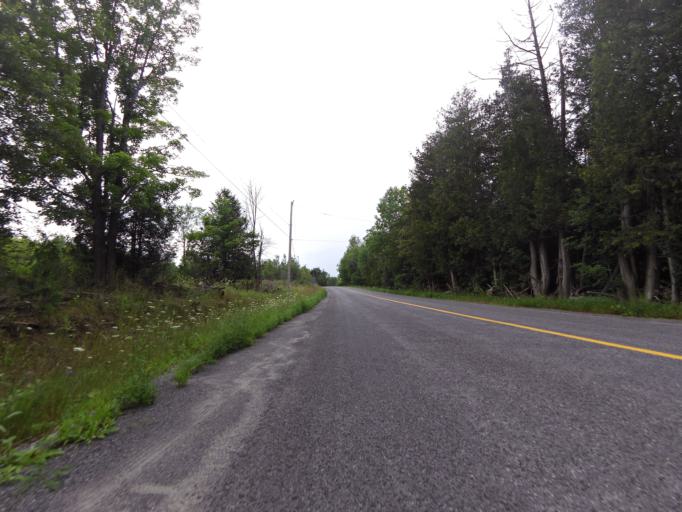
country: CA
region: Ontario
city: Perth
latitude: 44.8699
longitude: -76.5441
